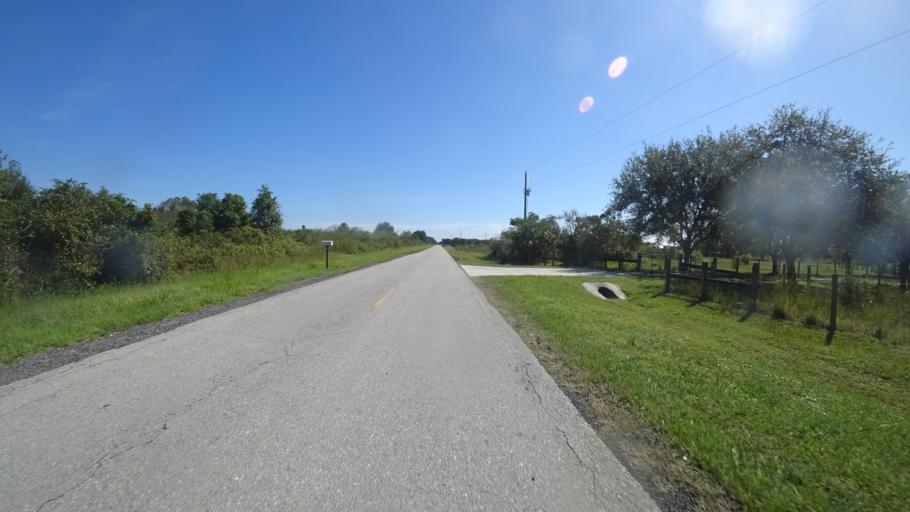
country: US
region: Florida
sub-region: Sarasota County
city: Warm Mineral Springs
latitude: 27.2736
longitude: -82.1524
